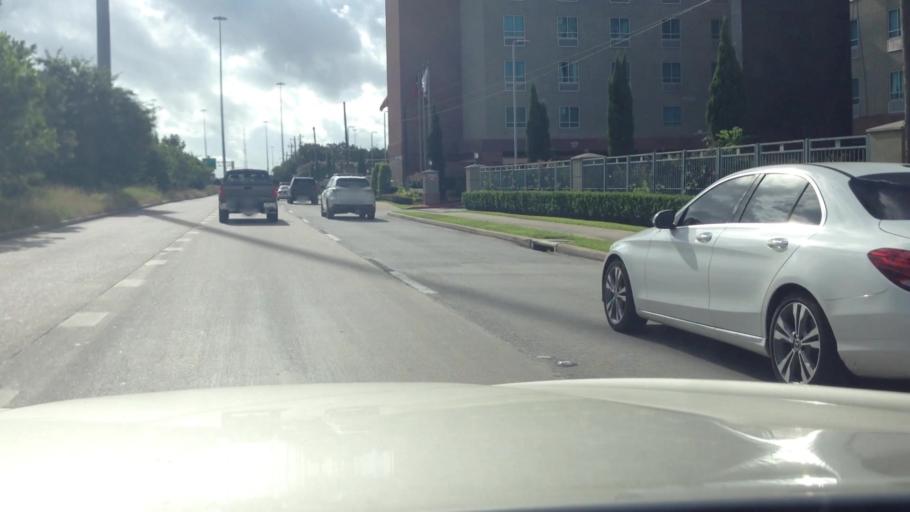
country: US
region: Texas
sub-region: Harris County
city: Hunters Creek Village
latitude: 29.7837
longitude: -95.4655
